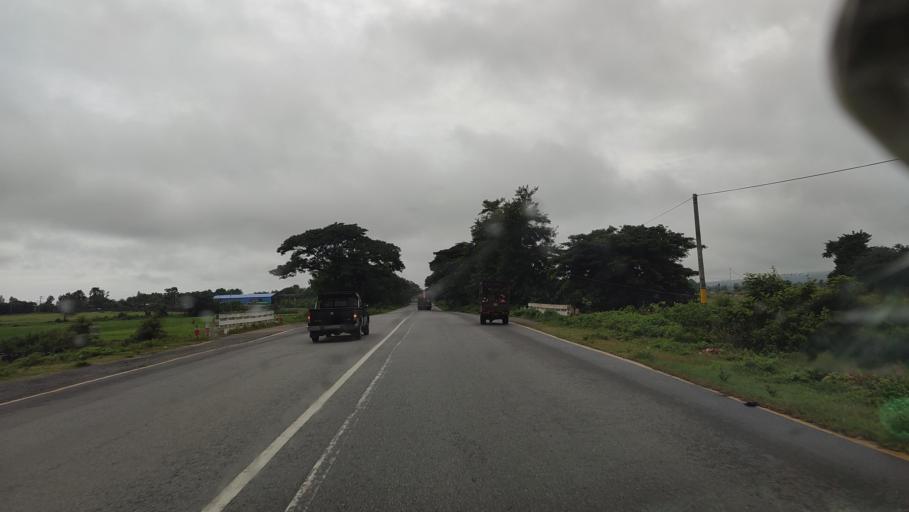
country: MM
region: Mandalay
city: Pyinmana
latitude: 19.9628
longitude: 96.2533
